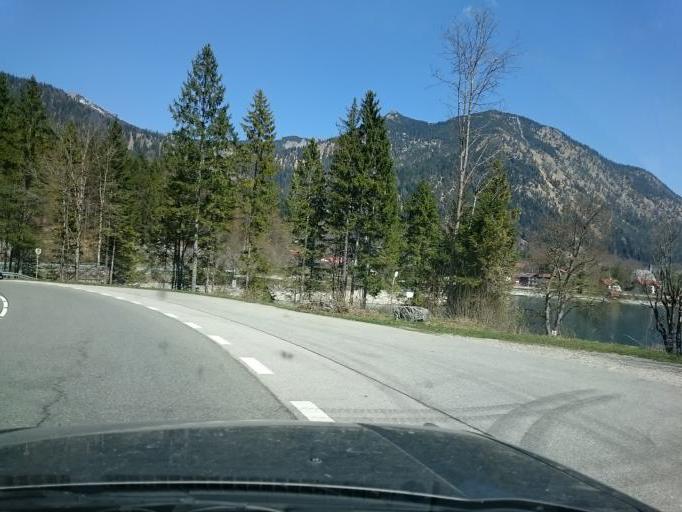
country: DE
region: Bavaria
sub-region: Upper Bavaria
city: Schlehdorf
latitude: 47.5838
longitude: 11.3077
